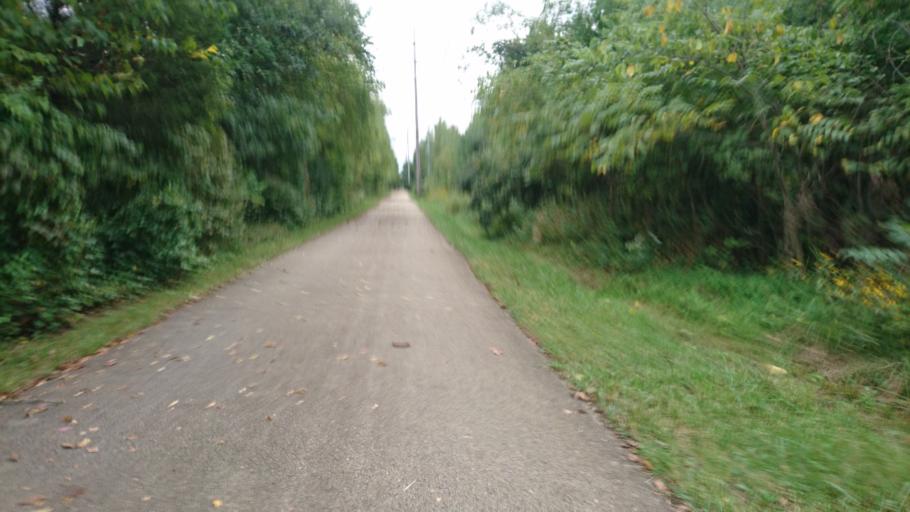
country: US
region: Illinois
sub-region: Sangamon County
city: Chatham
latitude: 39.7010
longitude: -89.6904
